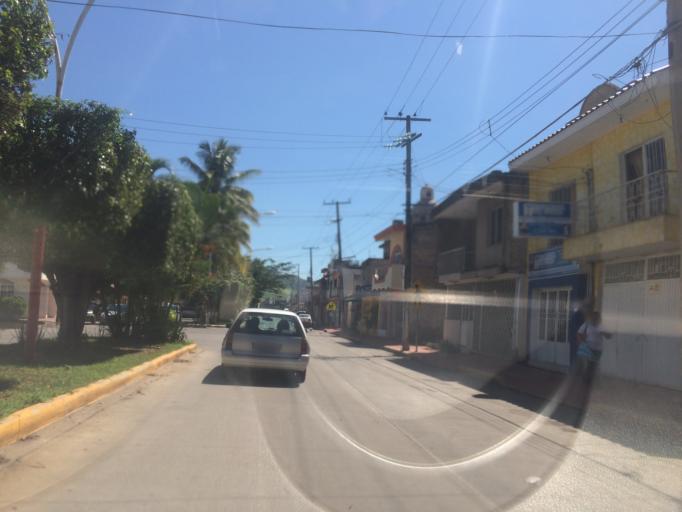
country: MX
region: Nayarit
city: Tepic
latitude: 21.4932
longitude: -104.8808
